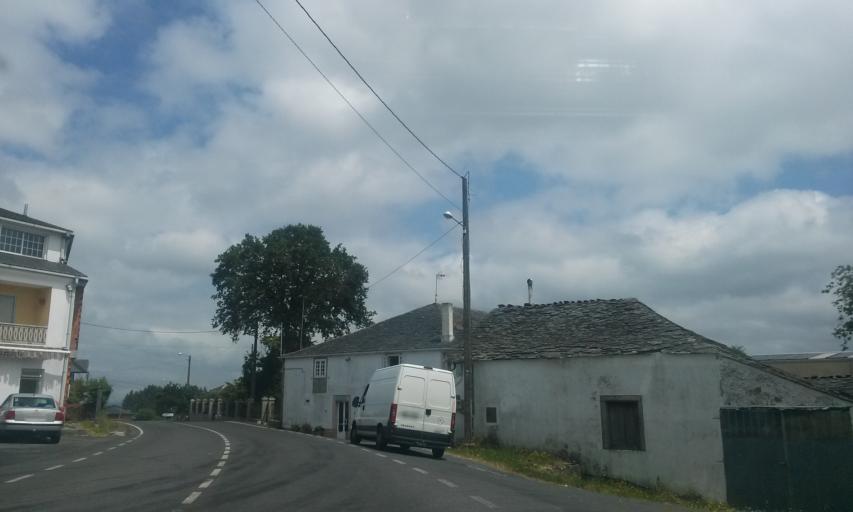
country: ES
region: Galicia
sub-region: Provincia de Lugo
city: Friol
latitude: 43.0607
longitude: -7.8369
